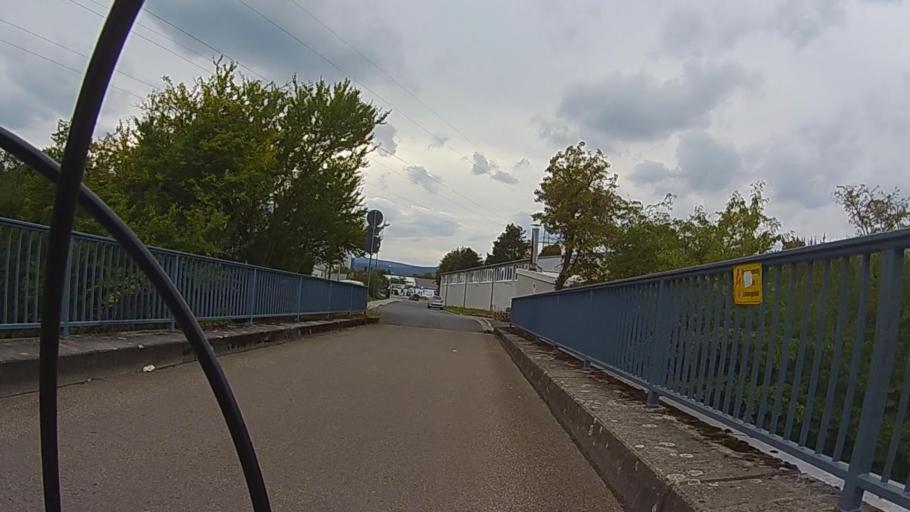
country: DE
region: Hesse
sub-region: Regierungsbezirk Darmstadt
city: Bad Homburg vor der Hoehe
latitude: 50.2137
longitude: 8.6071
